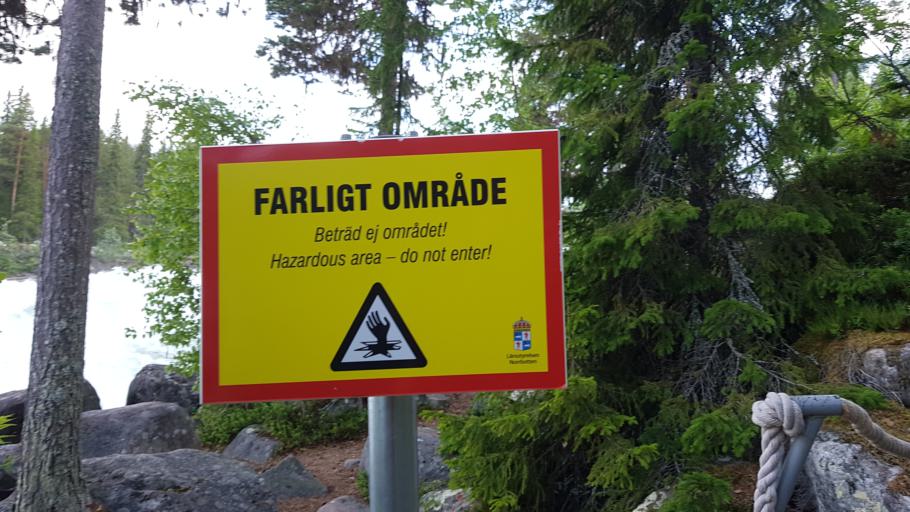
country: SE
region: Norrbotten
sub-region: Alvsbyns Kommun
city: AElvsbyn
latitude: 65.8535
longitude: 20.4132
